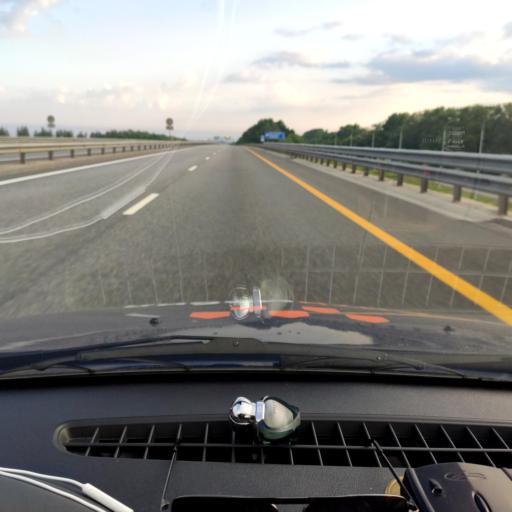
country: RU
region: Lipetsk
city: Zadonsk
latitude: 52.4601
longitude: 38.7747
